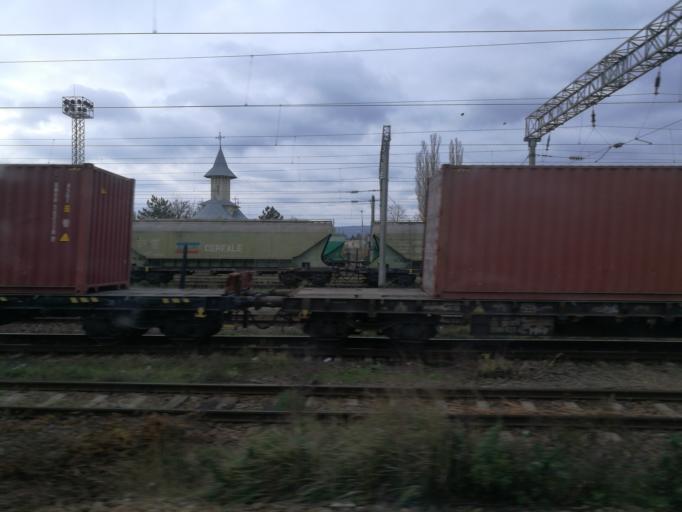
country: RO
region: Bacau
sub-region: Municipiul Bacau
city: Bacau
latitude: 46.5612
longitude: 26.8991
